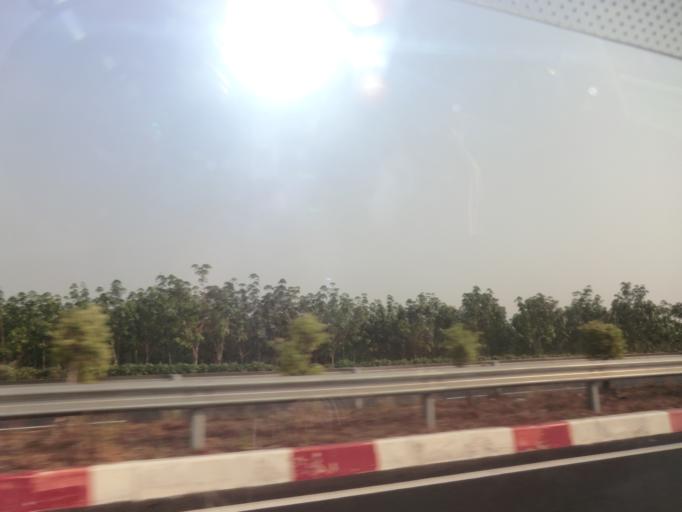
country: VN
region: Dong Nai
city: Long Thanh
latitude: 10.7782
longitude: 107.0120
